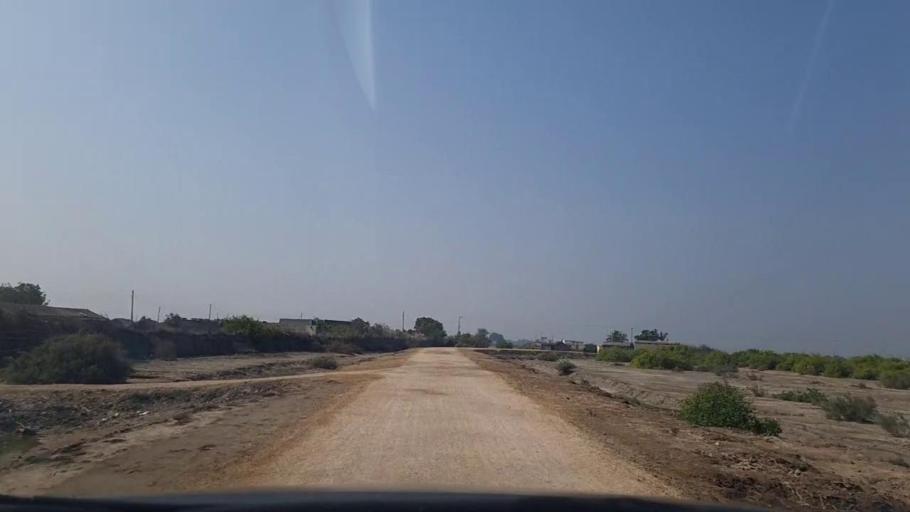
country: PK
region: Sindh
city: Mirpur Sakro
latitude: 24.5787
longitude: 67.7569
